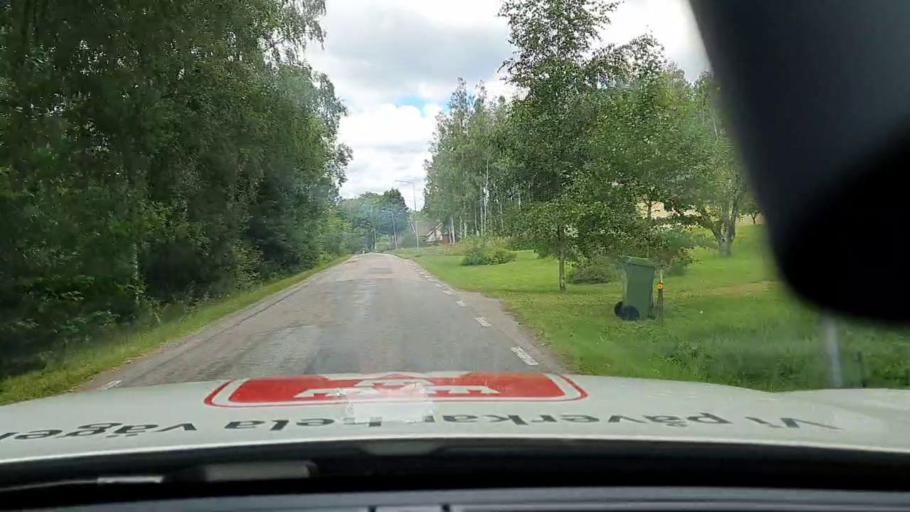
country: SE
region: Vaestra Goetaland
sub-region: Karlsborgs Kommun
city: Molltorp
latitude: 58.5814
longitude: 14.2699
